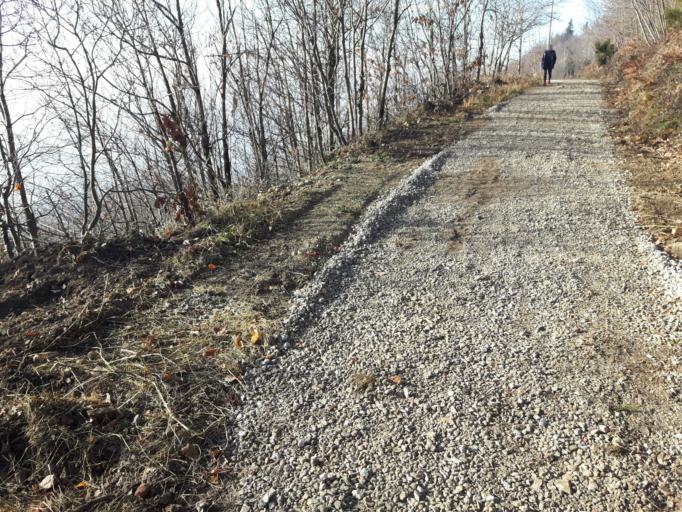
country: IT
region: Veneto
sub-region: Provincia di Padova
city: Fontanafredda
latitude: 45.3128
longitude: 11.6894
